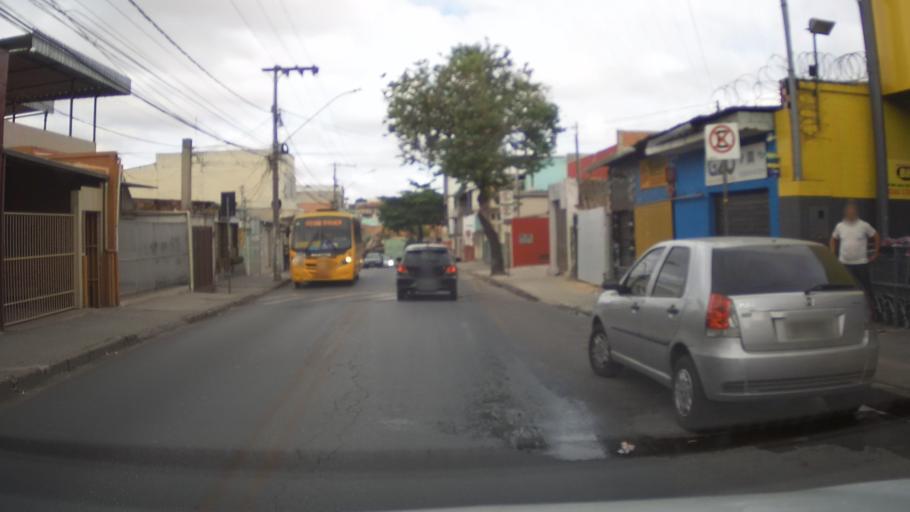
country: BR
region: Minas Gerais
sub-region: Belo Horizonte
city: Belo Horizonte
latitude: -19.8450
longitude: -43.9441
